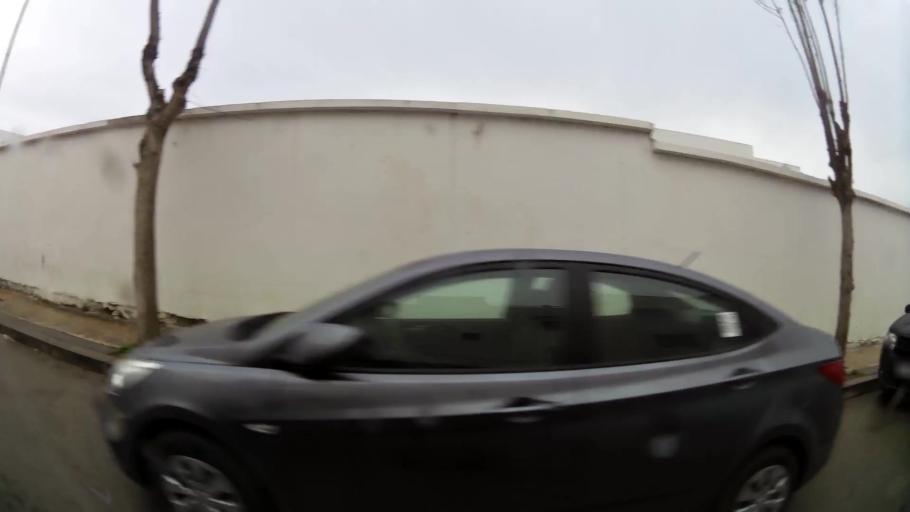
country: MA
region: Tanger-Tetouan
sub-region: Tetouan
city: Martil
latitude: 35.6204
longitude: -5.2774
